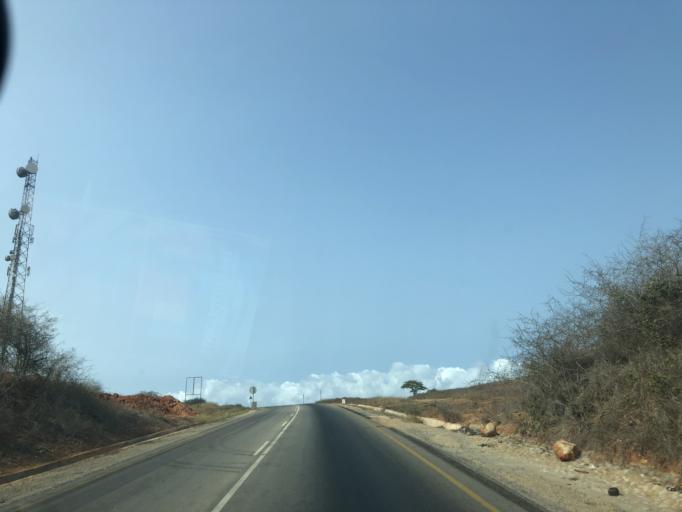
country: AO
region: Luanda
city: Luanda
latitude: -9.6926
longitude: 13.2124
